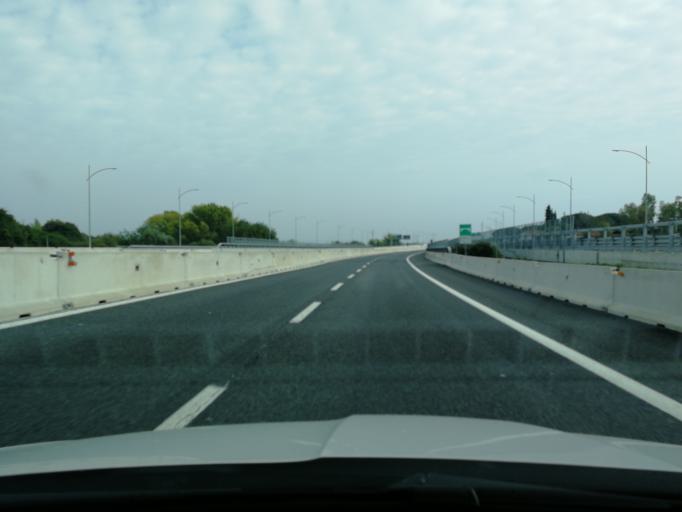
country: IT
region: Latium
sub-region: Citta metropolitana di Roma Capitale
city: Setteville
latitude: 41.9226
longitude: 12.6496
